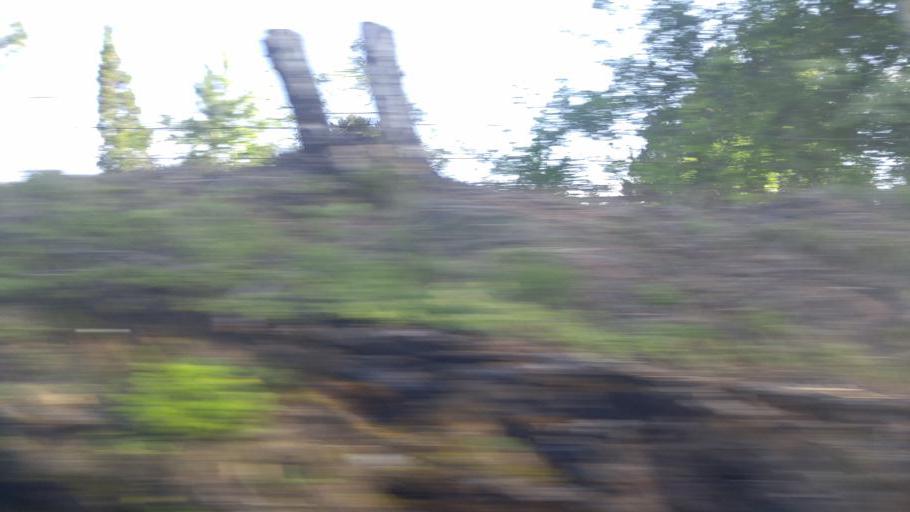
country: NO
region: Sor-Trondelag
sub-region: Malvik
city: Malvik
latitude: 63.4412
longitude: 10.6547
